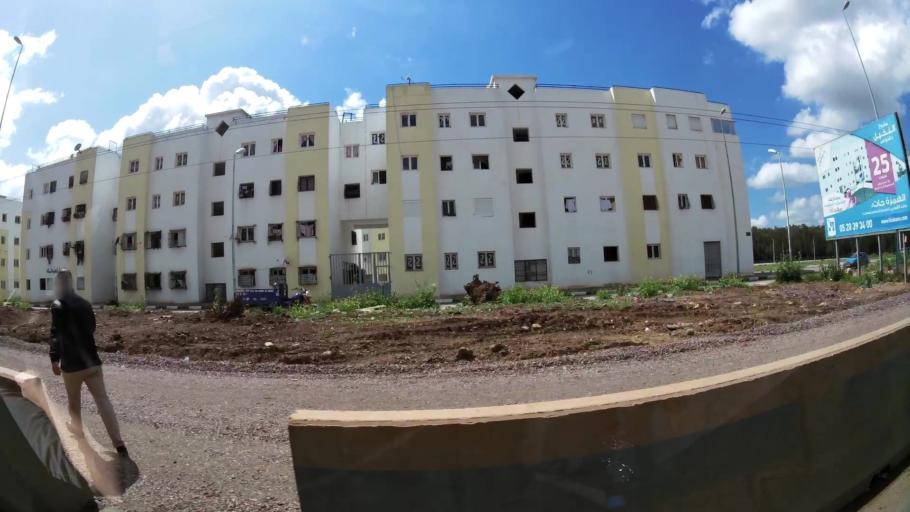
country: MA
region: Chaouia-Ouardigha
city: Nouaseur
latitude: 33.3664
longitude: -7.5441
